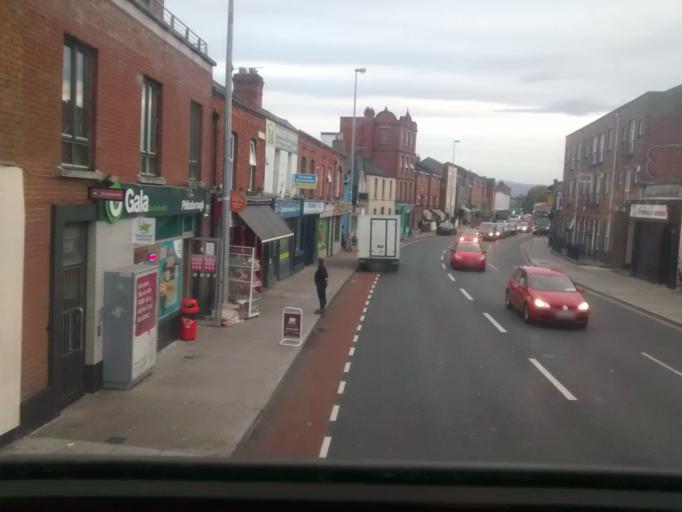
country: IE
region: Leinster
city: Glasnevin
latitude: 53.3601
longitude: -6.2726
